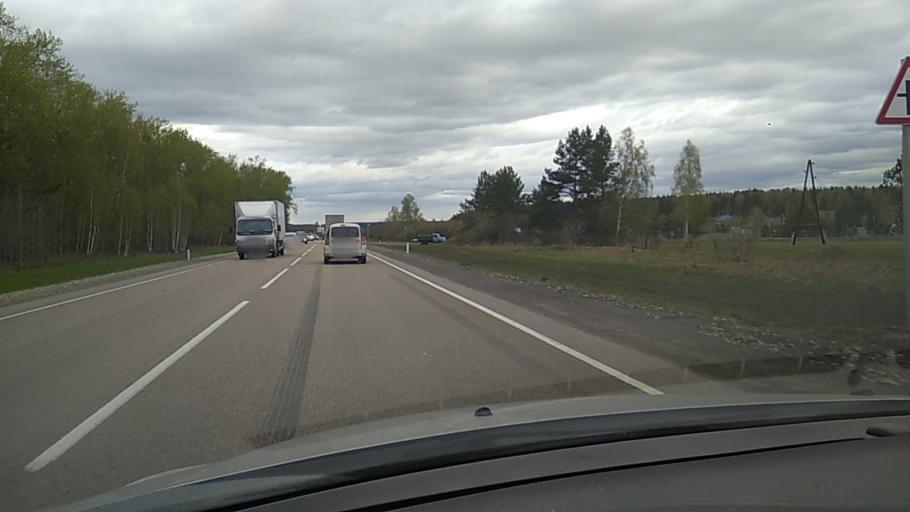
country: RU
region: Sverdlovsk
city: Dvurechensk
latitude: 56.6718
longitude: 61.1454
